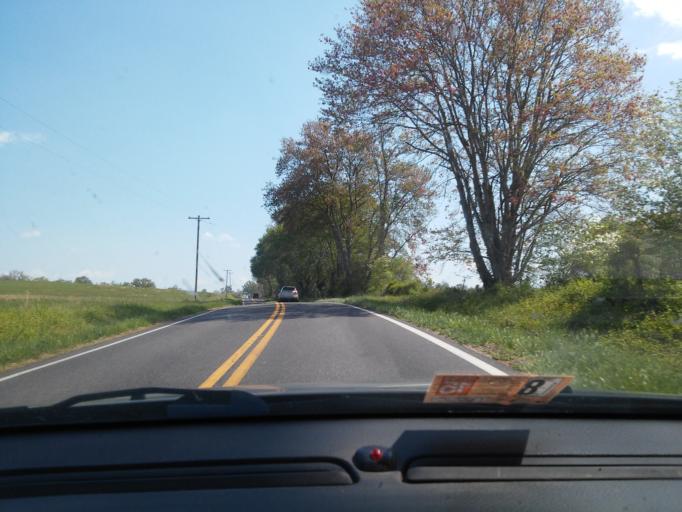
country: US
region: Virginia
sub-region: Rappahannock County
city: Washington
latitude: 38.5777
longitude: -78.2312
